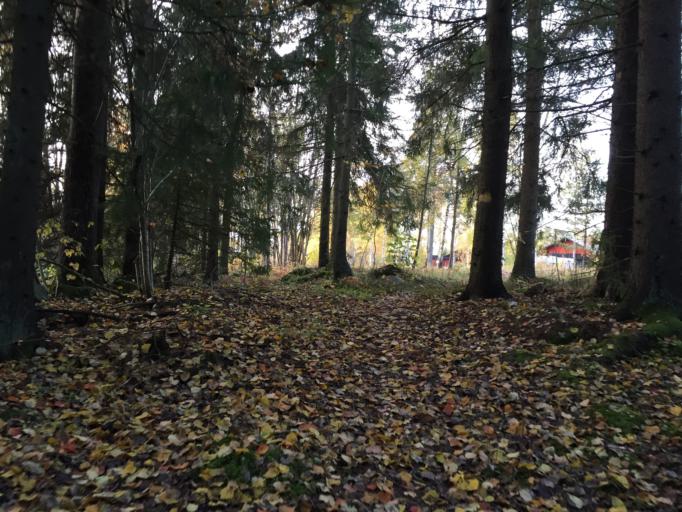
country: SE
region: Vaestmanland
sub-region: Hallstahammars Kommun
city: Hallstahammar
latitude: 59.6292
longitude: 16.2468
